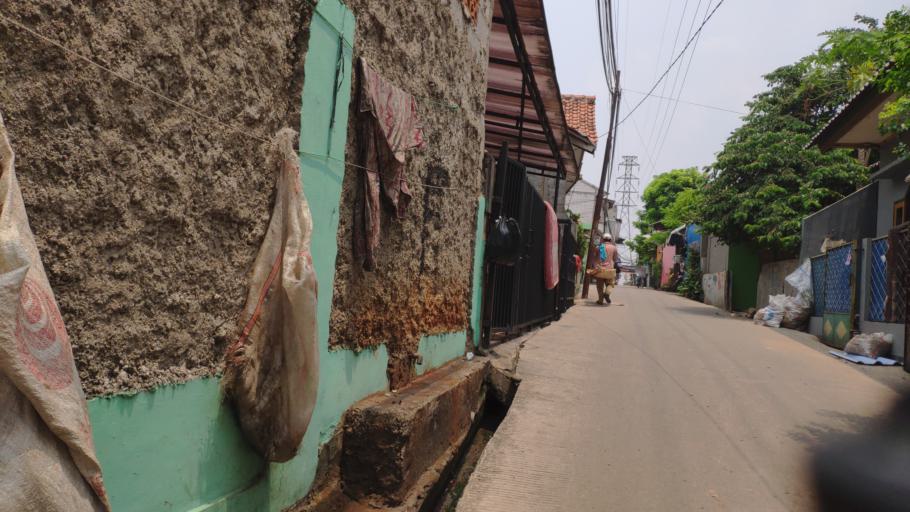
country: ID
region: West Java
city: Depok
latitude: -6.3092
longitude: 106.8310
